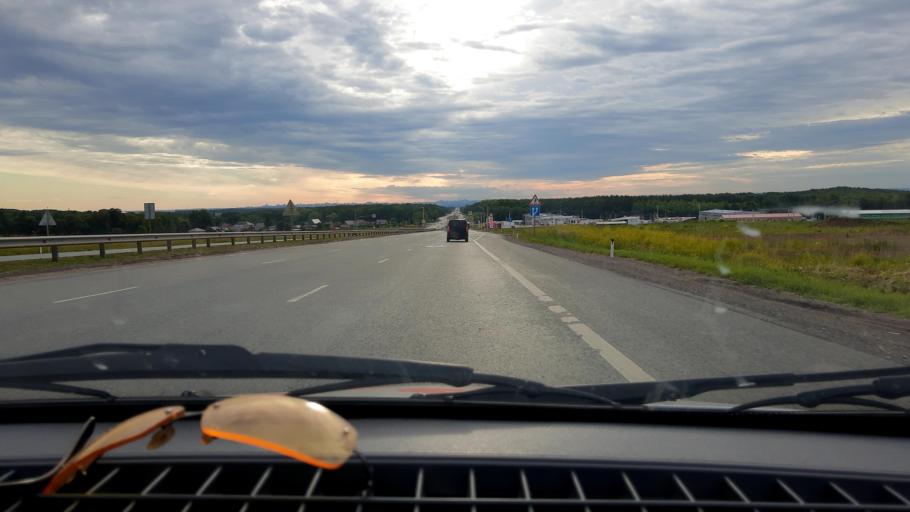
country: RU
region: Bashkortostan
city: Avdon
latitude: 54.6555
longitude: 55.6893
